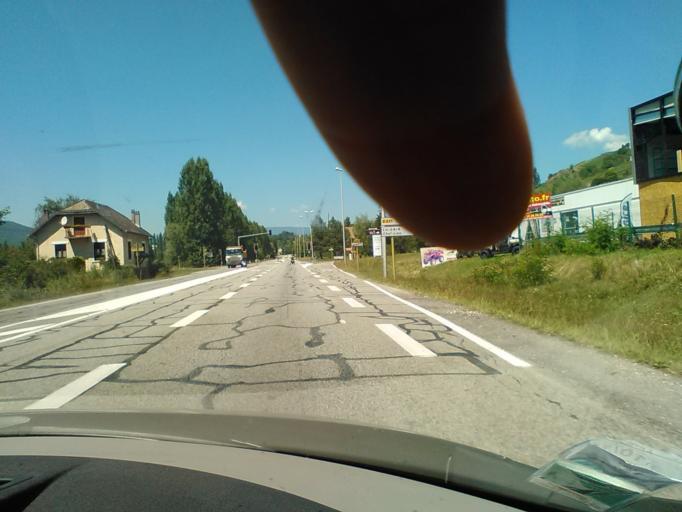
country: FR
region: Rhone-Alpes
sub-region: Departement de la Savoie
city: Les Marches
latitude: 45.5176
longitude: 6.0022
